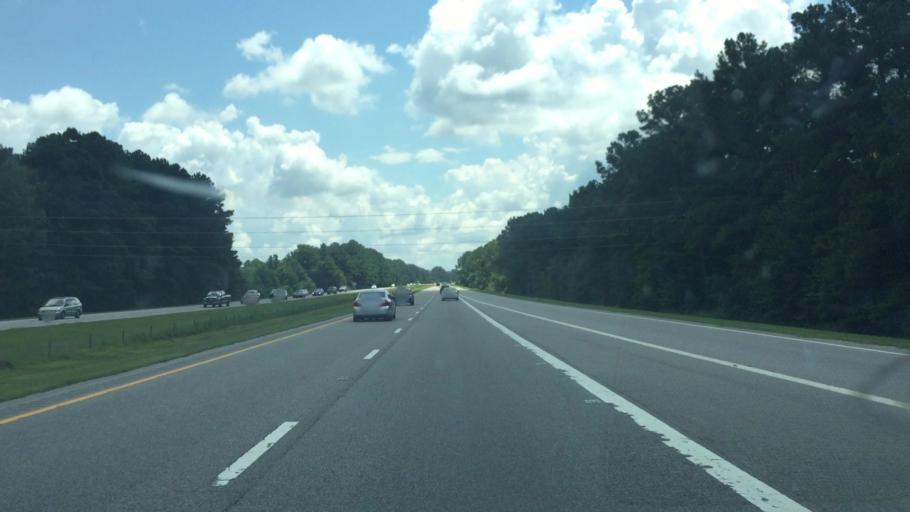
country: US
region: North Carolina
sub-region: Robeson County
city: Lumberton
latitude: 34.5780
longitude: -79.0454
